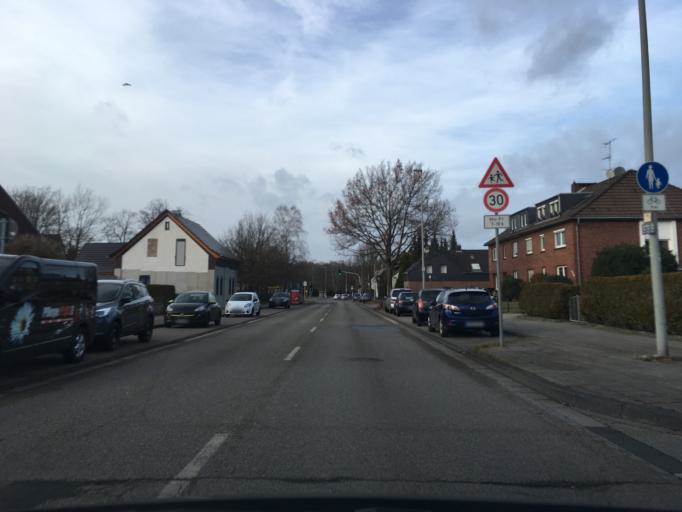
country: DE
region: North Rhine-Westphalia
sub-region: Regierungsbezirk Dusseldorf
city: Oberhausen
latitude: 51.5549
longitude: 6.8425
